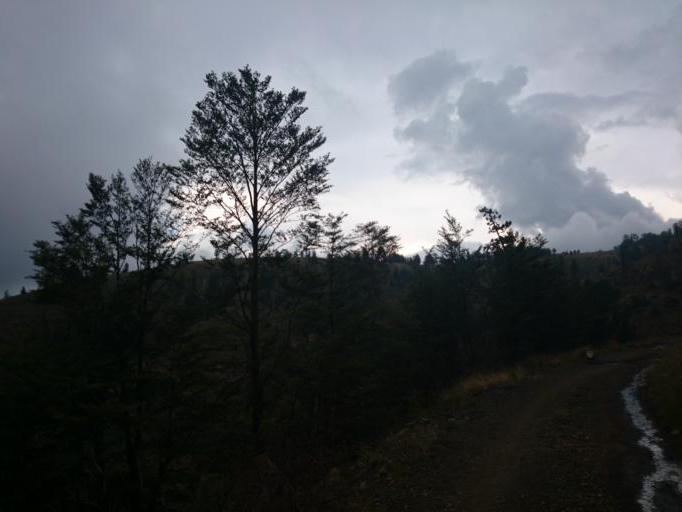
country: AL
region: Lezhe
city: Kurbnesh
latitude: 41.7843
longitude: 20.1543
